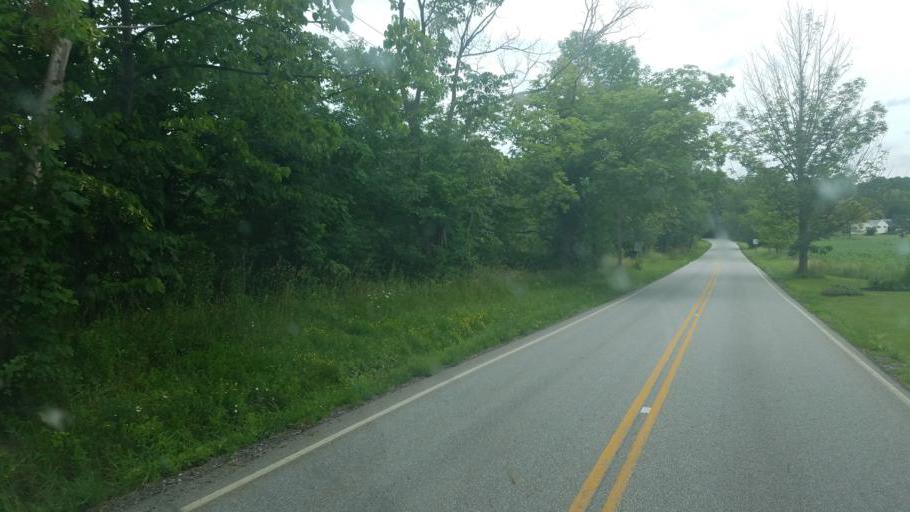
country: US
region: Ohio
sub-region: Geauga County
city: Burton
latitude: 41.4807
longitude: -81.2048
